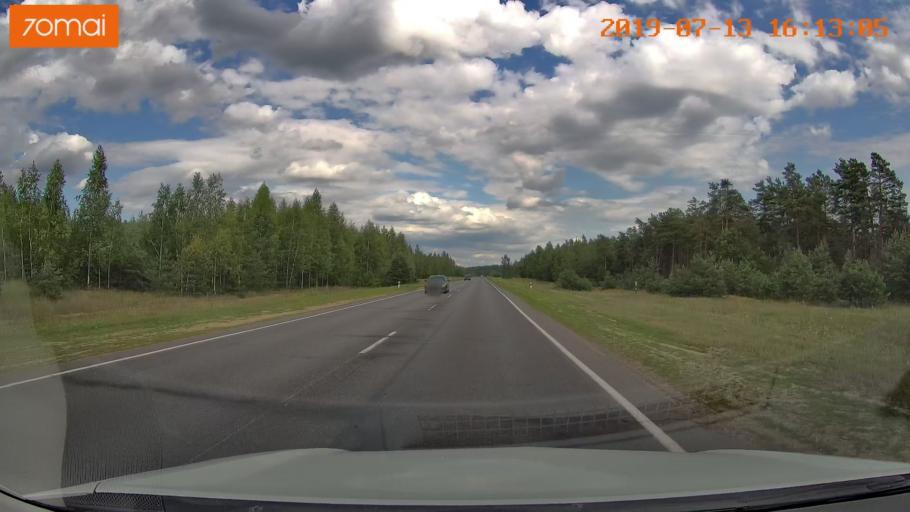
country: BY
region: Mogilev
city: Babruysk
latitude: 53.1644
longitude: 29.2953
